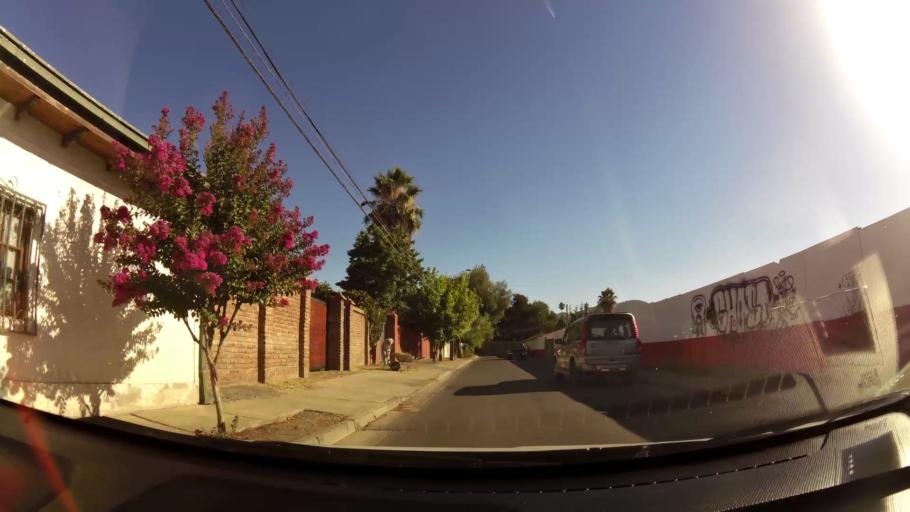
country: CL
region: O'Higgins
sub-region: Provincia de Colchagua
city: Chimbarongo
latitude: -34.5933
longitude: -70.9933
